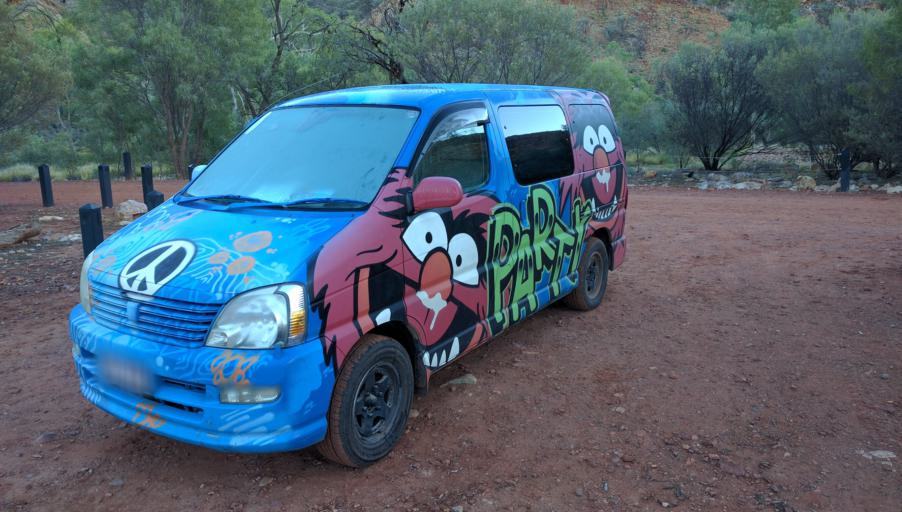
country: AU
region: Northern Territory
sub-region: Alice Springs
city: Alice Springs
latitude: -23.7804
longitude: 133.0723
